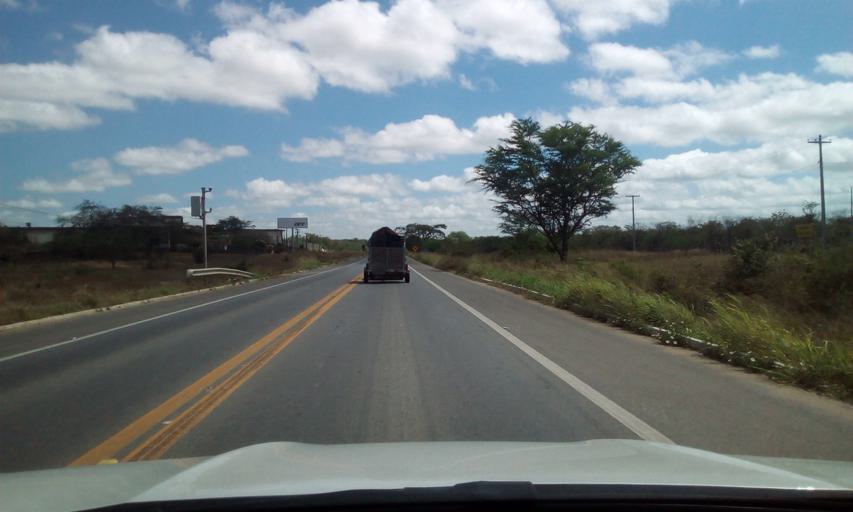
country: BR
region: Paraiba
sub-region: Campina Grande
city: Campina Grande
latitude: -7.3275
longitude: -35.8969
